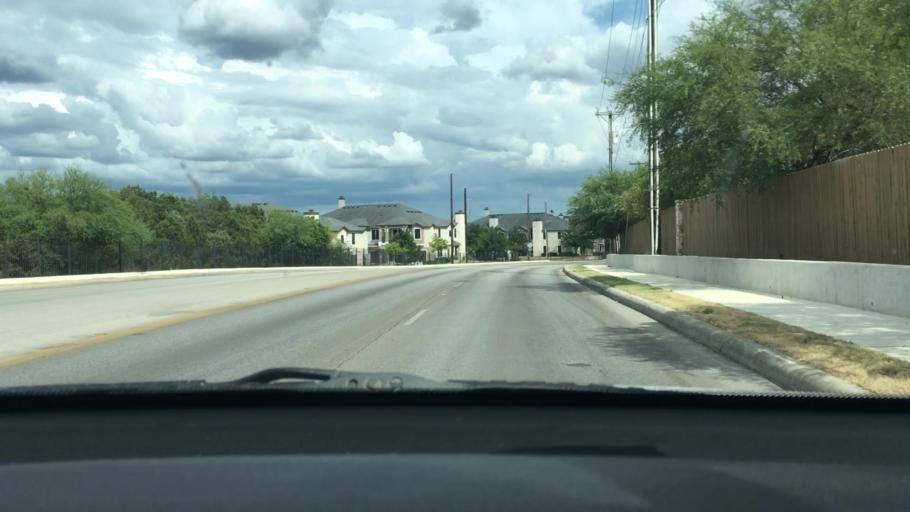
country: US
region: Texas
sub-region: Bexar County
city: Timberwood Park
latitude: 29.6539
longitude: -98.4281
